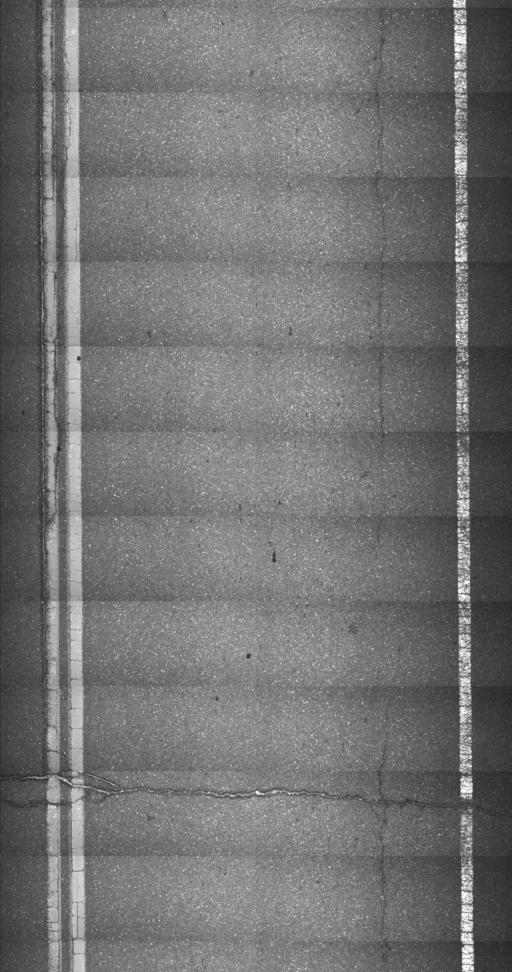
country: US
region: Vermont
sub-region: Orleans County
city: Newport
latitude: 45.0018
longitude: -72.1020
